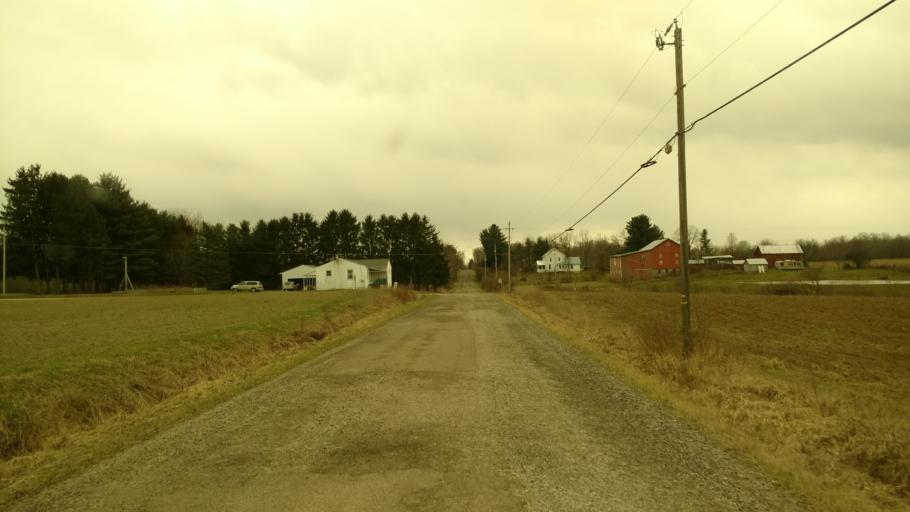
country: US
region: Ohio
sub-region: Crawford County
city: Galion
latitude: 40.6695
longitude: -82.7939
